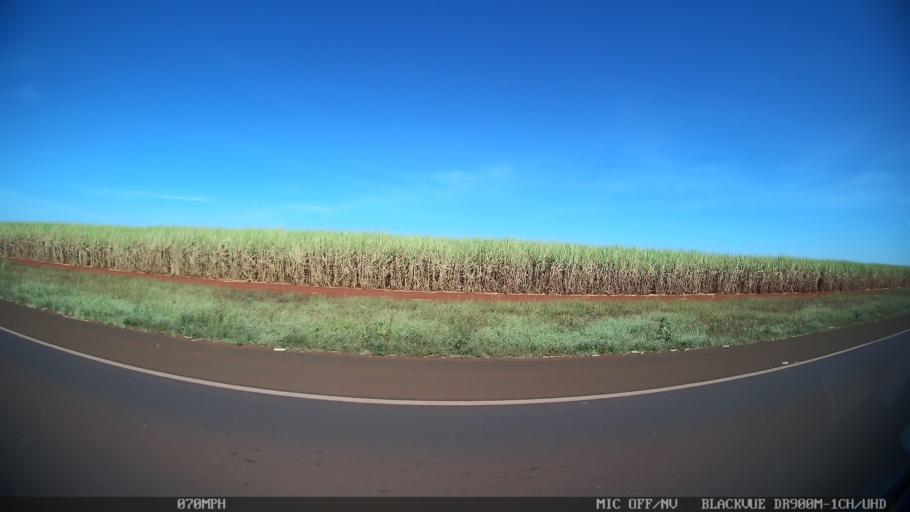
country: BR
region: Sao Paulo
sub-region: Guaira
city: Guaira
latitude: -20.4444
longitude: -48.2761
